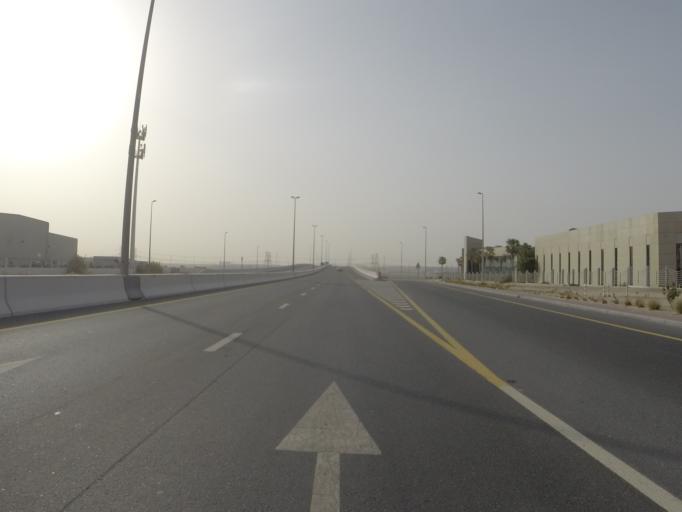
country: AE
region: Dubai
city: Dubai
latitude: 24.9596
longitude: 55.0969
